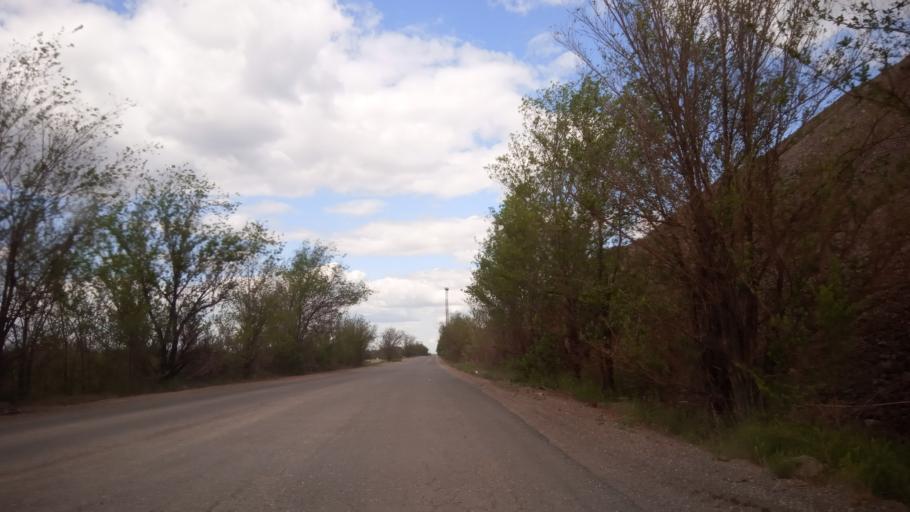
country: RU
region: Orenburg
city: Novotroitsk
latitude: 51.2463
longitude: 58.3604
